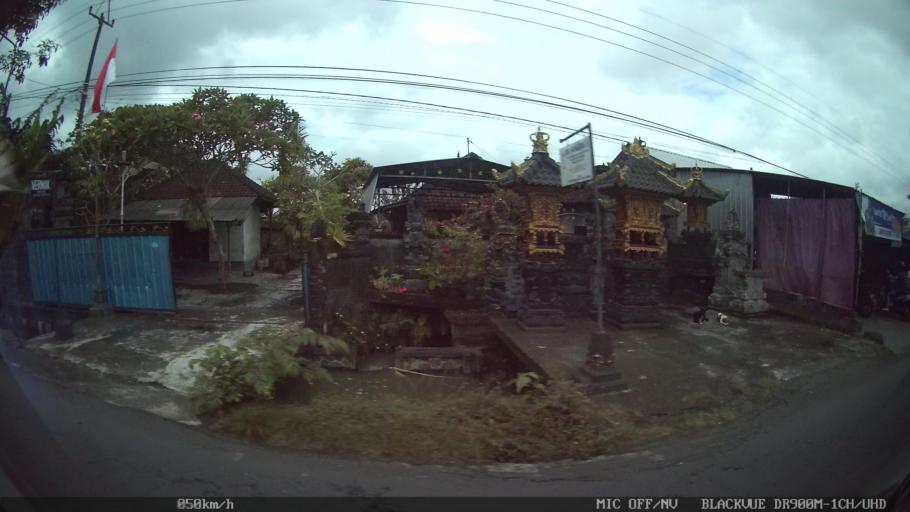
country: ID
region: Bali
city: Banjar Pekenjelodan
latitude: -8.5603
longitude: 115.1882
